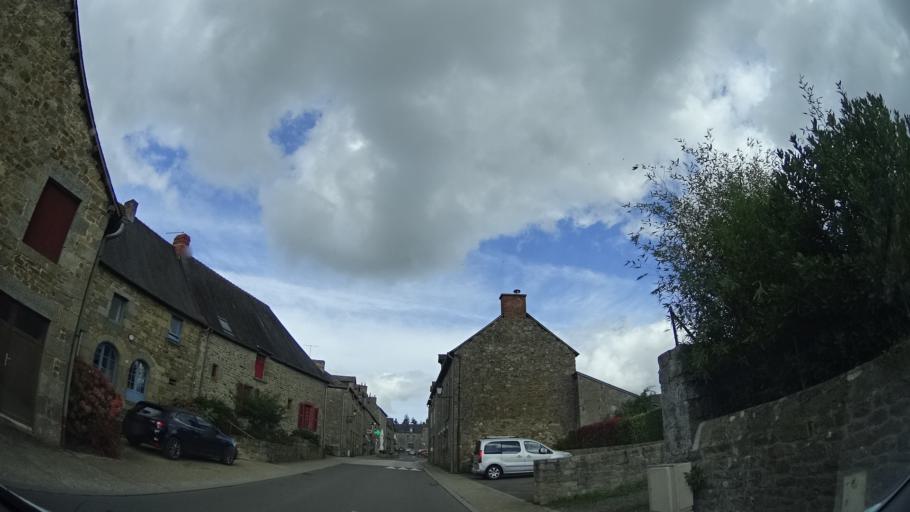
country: FR
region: Brittany
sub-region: Departement d'Ille-et-Vilaine
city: Dinge
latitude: 48.3564
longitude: -1.7140
